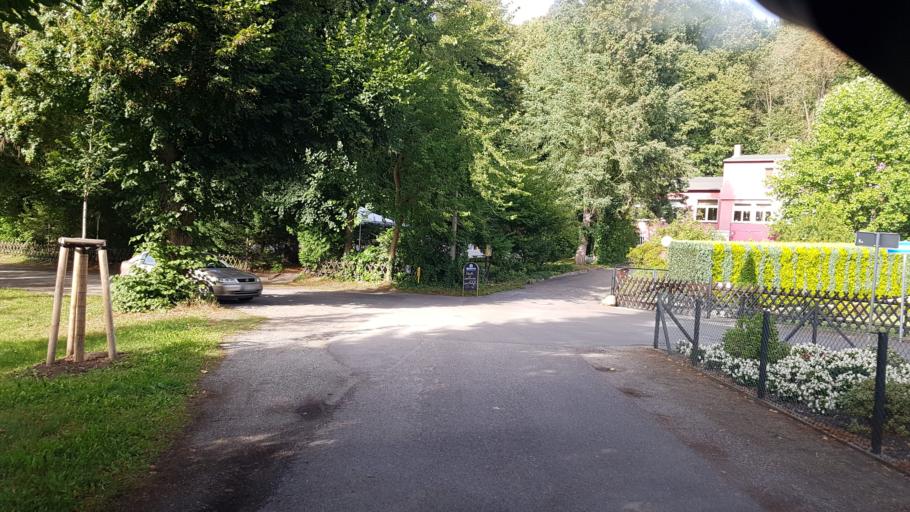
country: DE
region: Brandenburg
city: Spremberg
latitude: 51.5701
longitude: 14.3848
